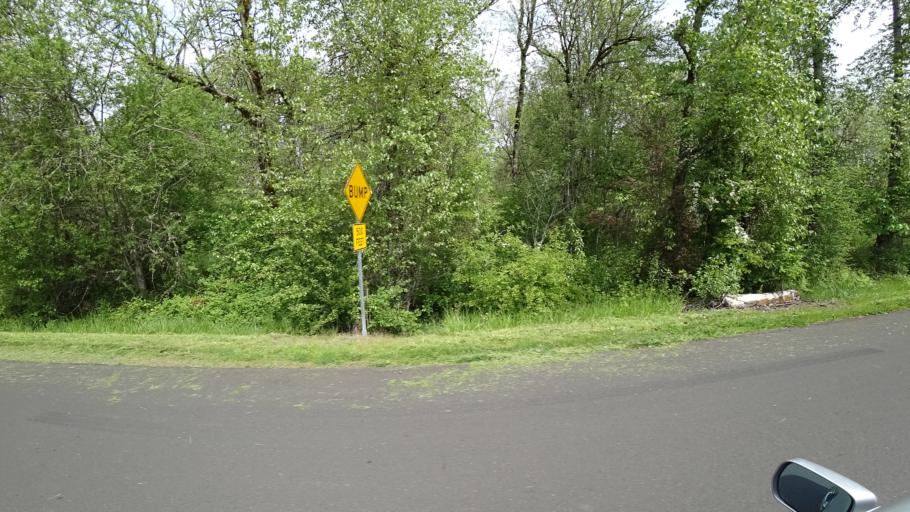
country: US
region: Oregon
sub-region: Washington County
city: Hillsboro
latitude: 45.5326
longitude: -123.0037
